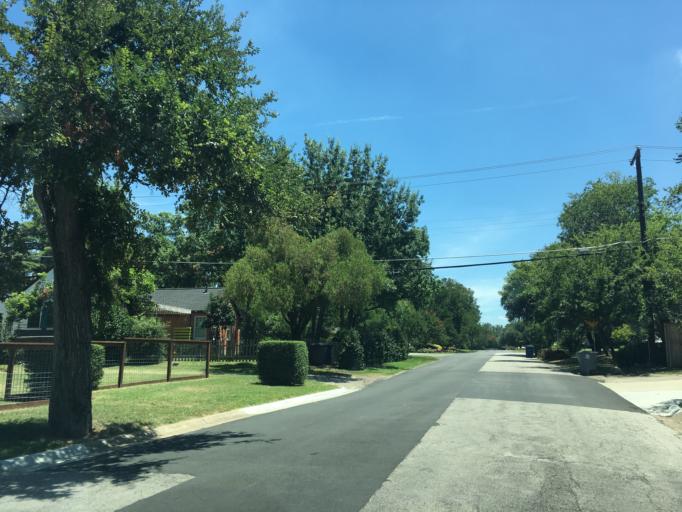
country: US
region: Texas
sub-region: Dallas County
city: Highland Park
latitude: 32.8338
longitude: -96.6977
